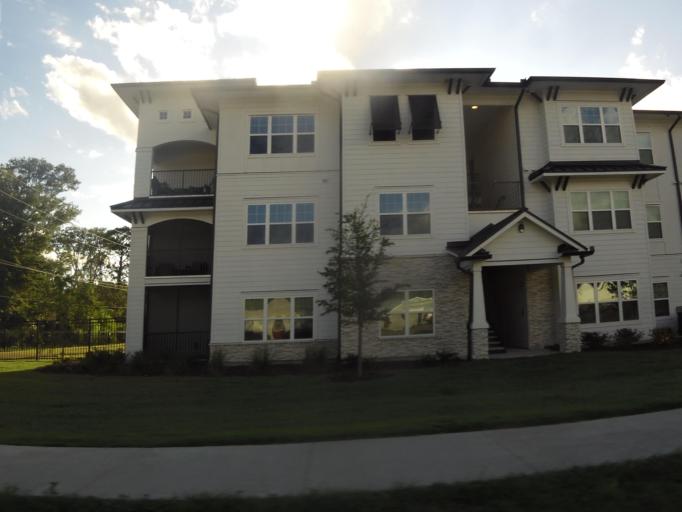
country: US
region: Florida
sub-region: Nassau County
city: Fernandina Beach
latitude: 30.6528
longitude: -81.4542
